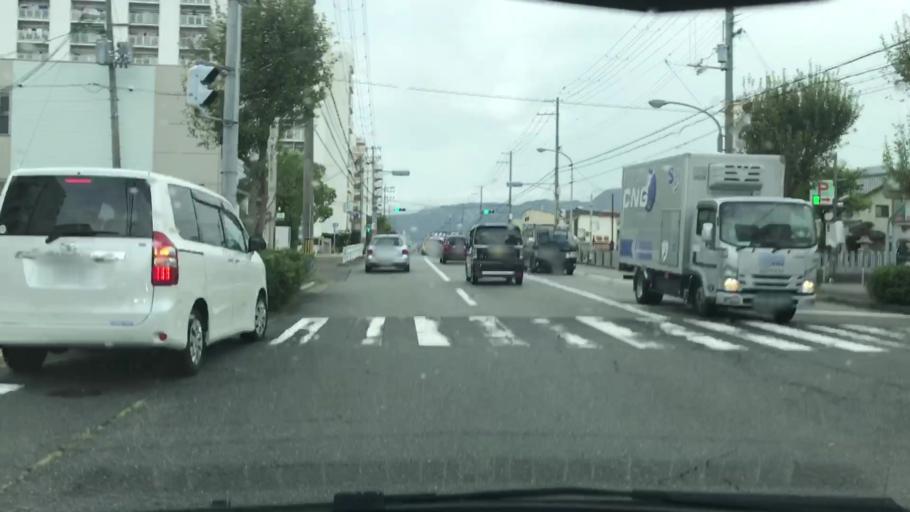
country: JP
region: Hyogo
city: Nishinomiya-hama
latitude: 34.7422
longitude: 135.3504
